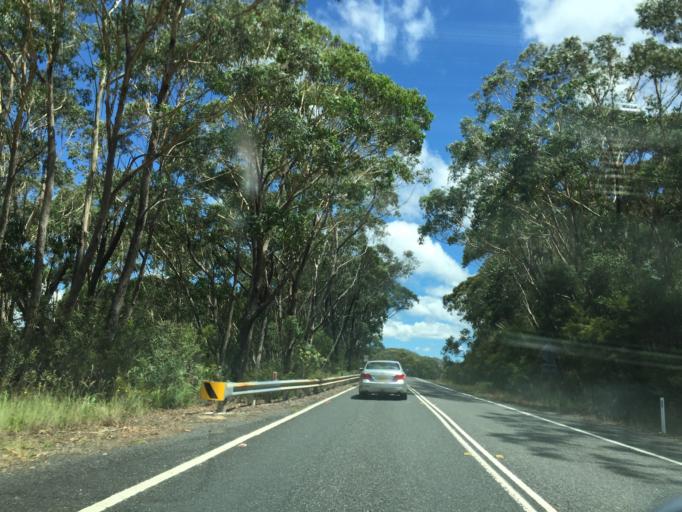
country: AU
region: New South Wales
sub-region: Blue Mountains Municipality
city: Blackheath
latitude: -33.5457
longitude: 150.3857
